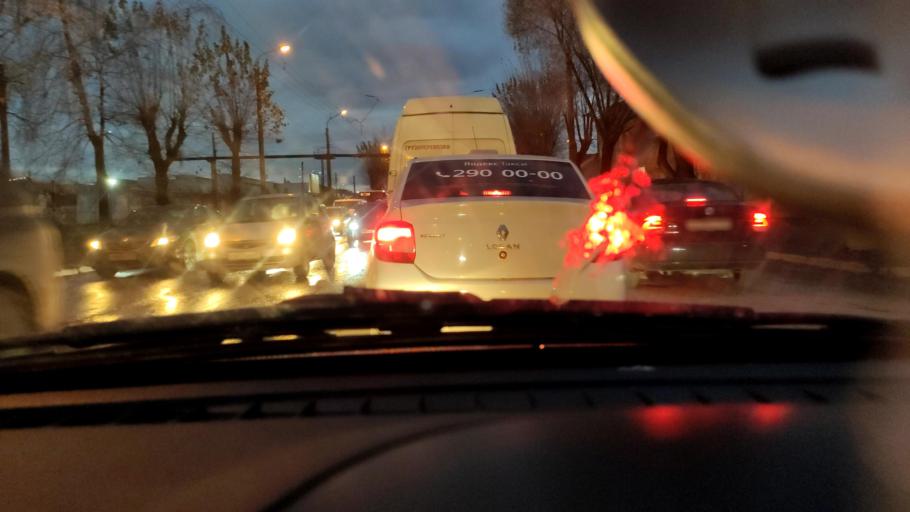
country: RU
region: Perm
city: Perm
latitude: 57.9762
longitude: 56.2464
